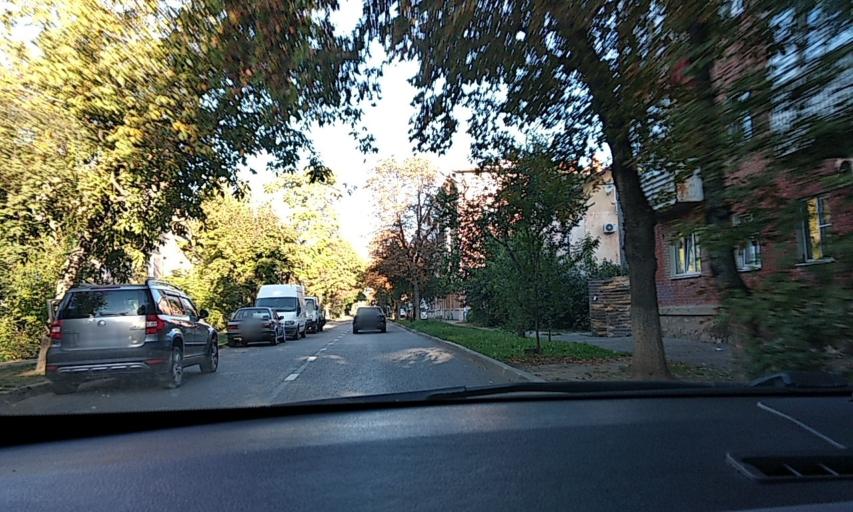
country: RU
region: Adygeya
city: Yablonovskiy
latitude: 45.0100
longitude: 38.9638
